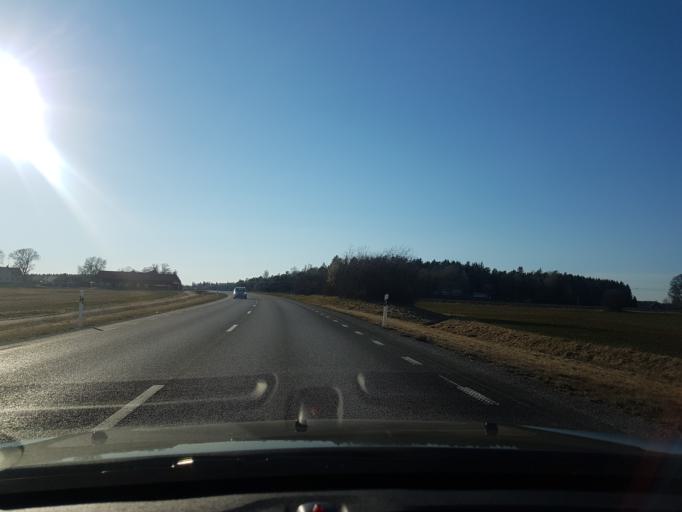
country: SE
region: Uppsala
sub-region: Enkopings Kommun
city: Orsundsbro
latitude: 59.8582
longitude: 17.4212
